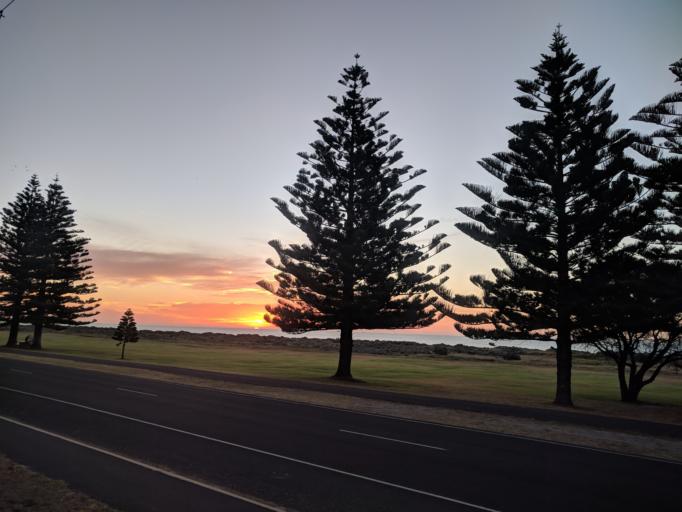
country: AU
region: South Australia
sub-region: Tatiara
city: Keith
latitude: -36.8367
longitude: 139.8458
